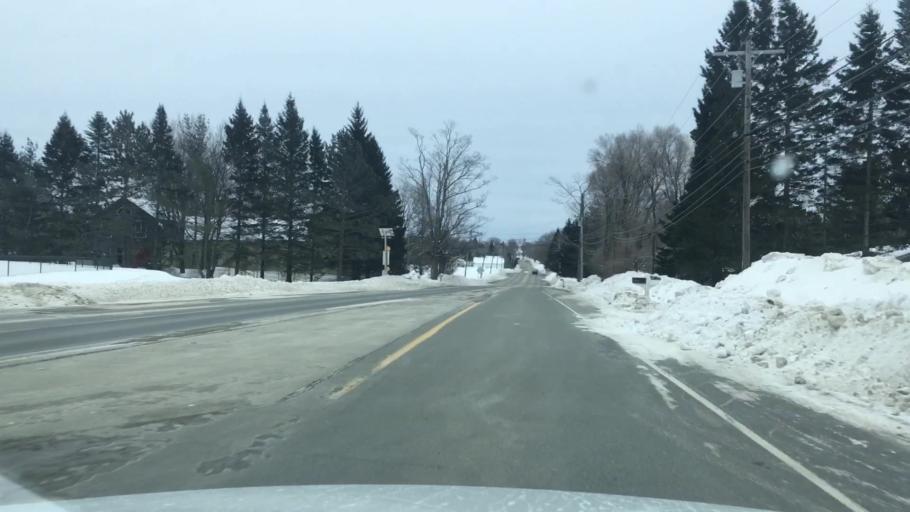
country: US
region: Maine
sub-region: Penobscot County
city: Charleston
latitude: 45.0163
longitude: -69.0278
